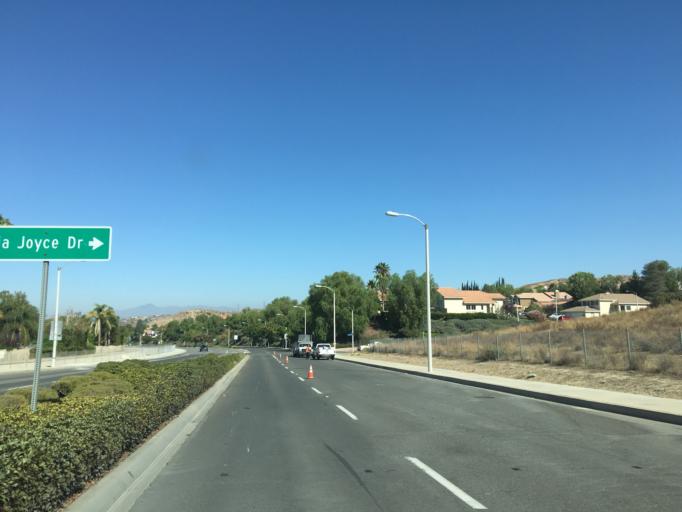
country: US
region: California
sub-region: Los Angeles County
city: Santa Clarita
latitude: 34.4470
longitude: -118.4891
